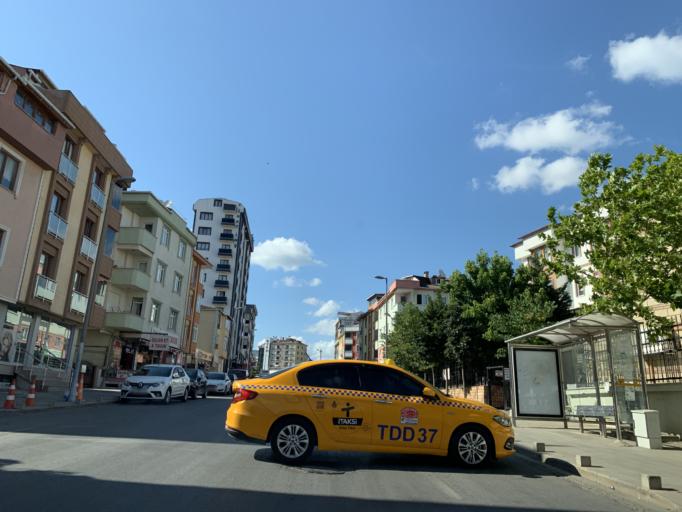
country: TR
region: Istanbul
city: Pendik
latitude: 40.8877
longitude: 29.2729
